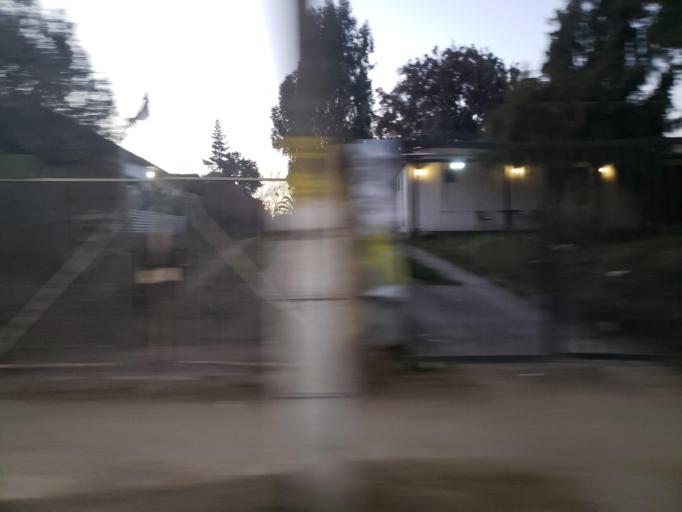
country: CL
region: Santiago Metropolitan
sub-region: Provincia de Talagante
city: El Monte
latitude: -33.6829
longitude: -70.9872
